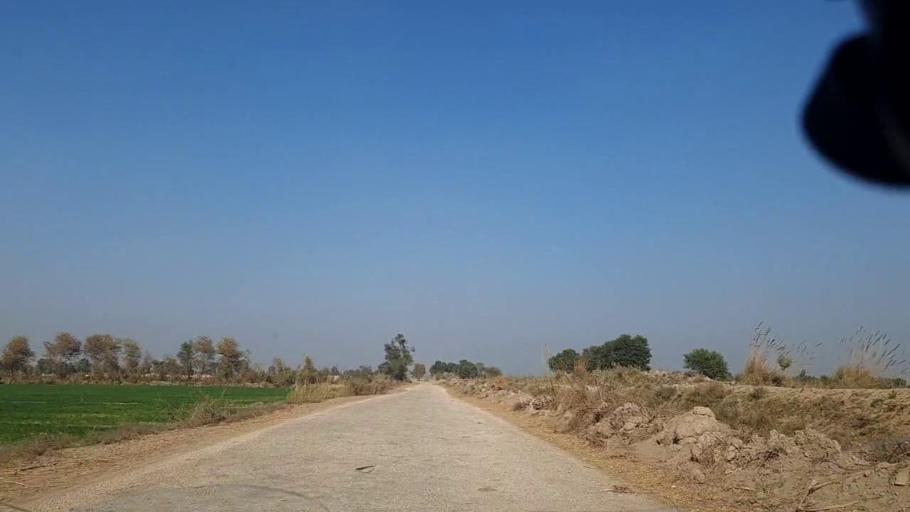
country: PK
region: Sindh
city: Khanpur
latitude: 27.6868
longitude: 69.4955
